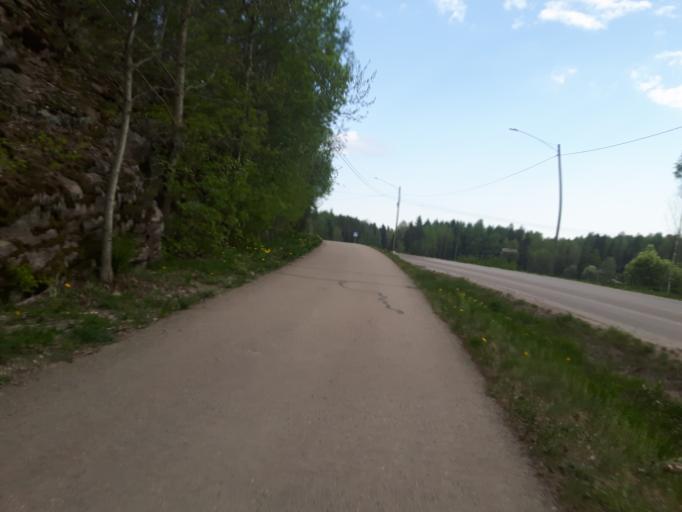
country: FI
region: Uusimaa
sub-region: Porvoo
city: Porvoo
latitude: 60.3959
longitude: 25.7336
